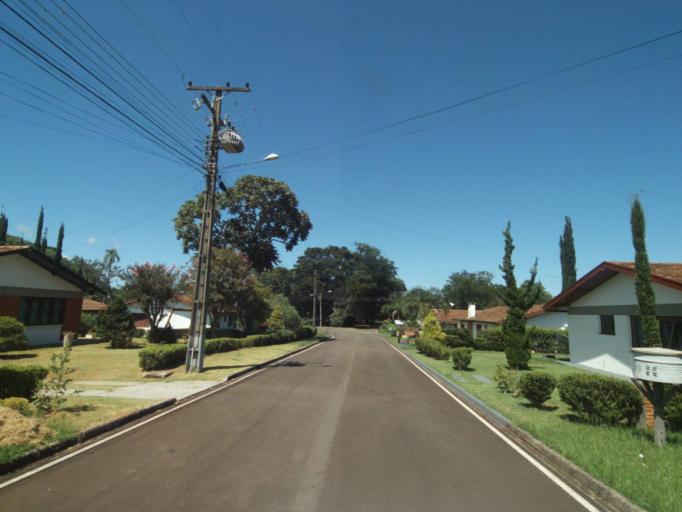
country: BR
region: Parana
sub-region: Chopinzinho
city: Chopinzinho
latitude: -25.7982
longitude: -52.0965
